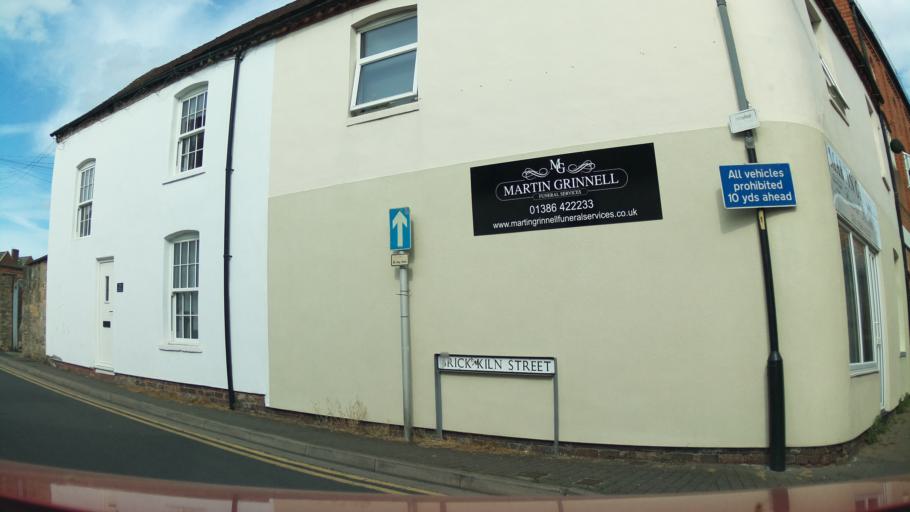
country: GB
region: England
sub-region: Worcestershire
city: Evesham
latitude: 52.0928
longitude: -1.9484
